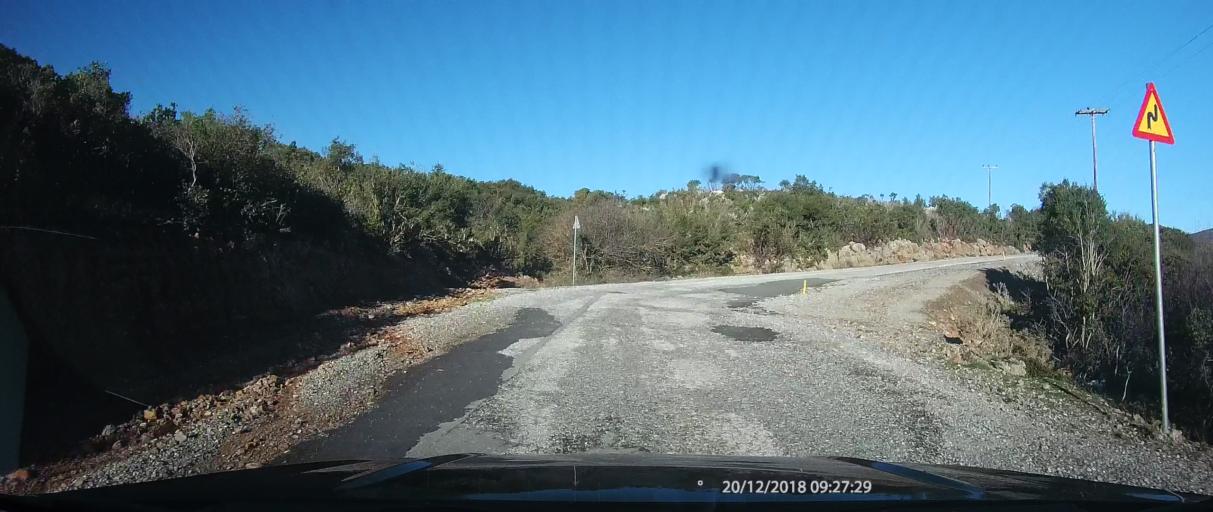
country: GR
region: Peloponnese
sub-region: Nomos Lakonias
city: Kato Glikovrisi
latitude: 36.9599
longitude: 22.8640
